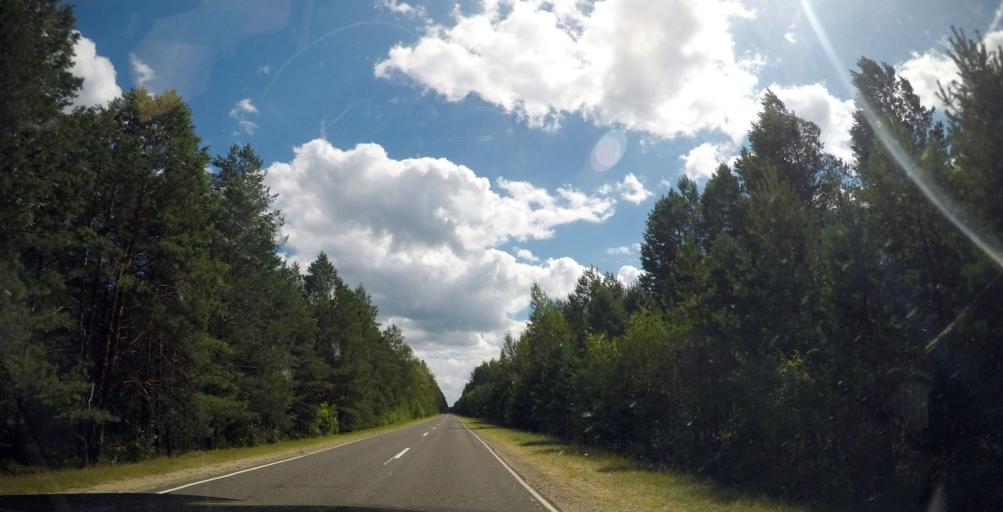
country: LT
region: Alytaus apskritis
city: Druskininkai
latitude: 53.8607
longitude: 24.1782
